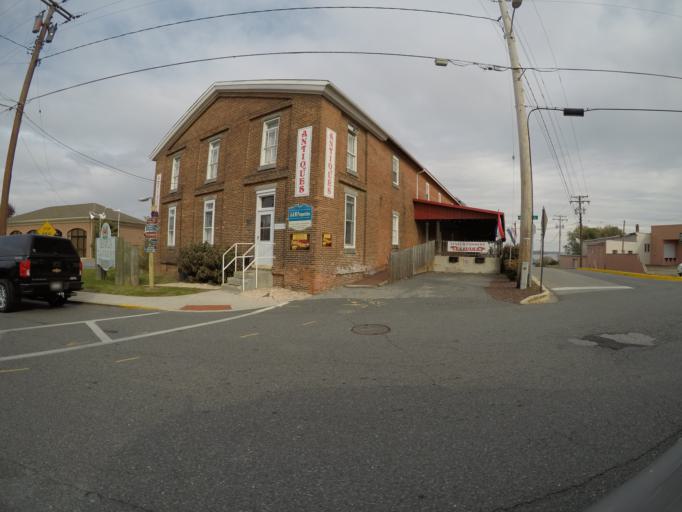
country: US
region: Maryland
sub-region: Harford County
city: Havre de Grace
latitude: 39.5490
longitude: -76.0889
